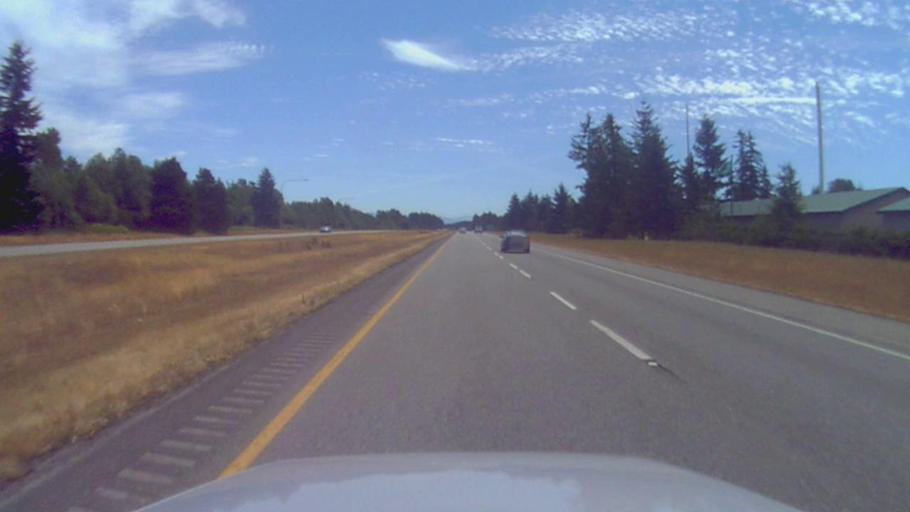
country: US
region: Washington
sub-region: Whatcom County
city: Ferndale
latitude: 48.8977
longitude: -122.6066
